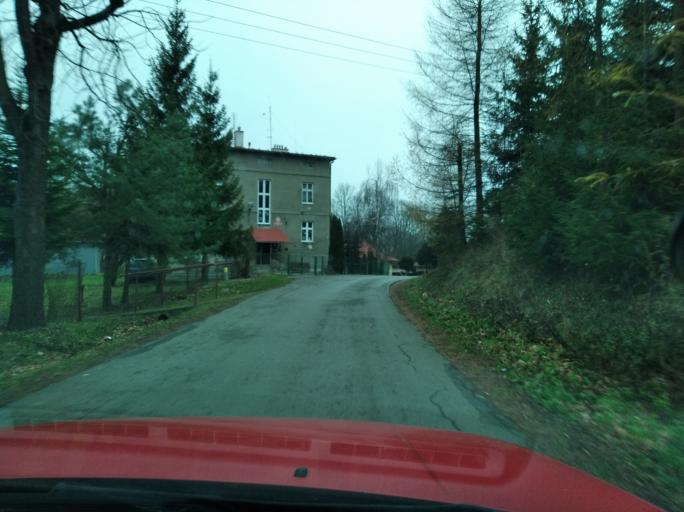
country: PL
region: Subcarpathian Voivodeship
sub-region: Powiat jaroslawski
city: Wierzbna
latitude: 50.0186
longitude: 22.6260
